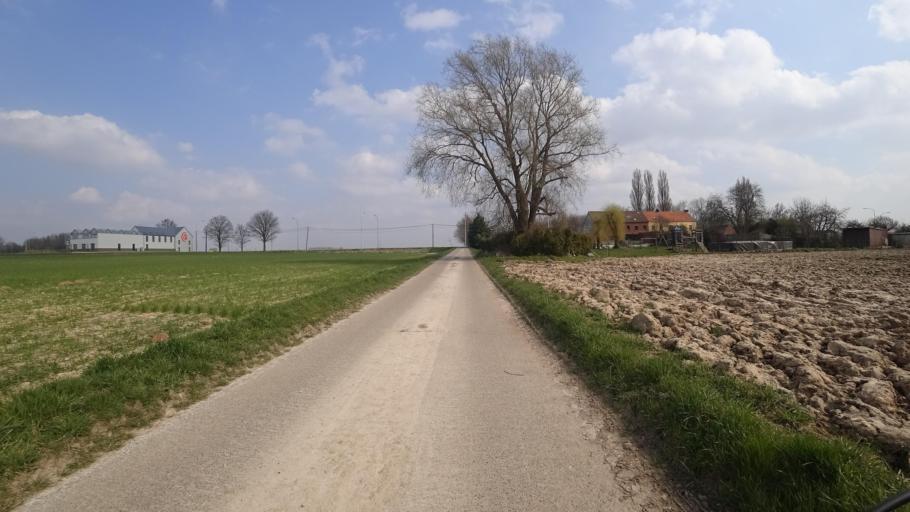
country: BE
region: Wallonia
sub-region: Province du Brabant Wallon
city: Chastre-Villeroux-Blanmont
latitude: 50.6167
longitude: 4.6615
